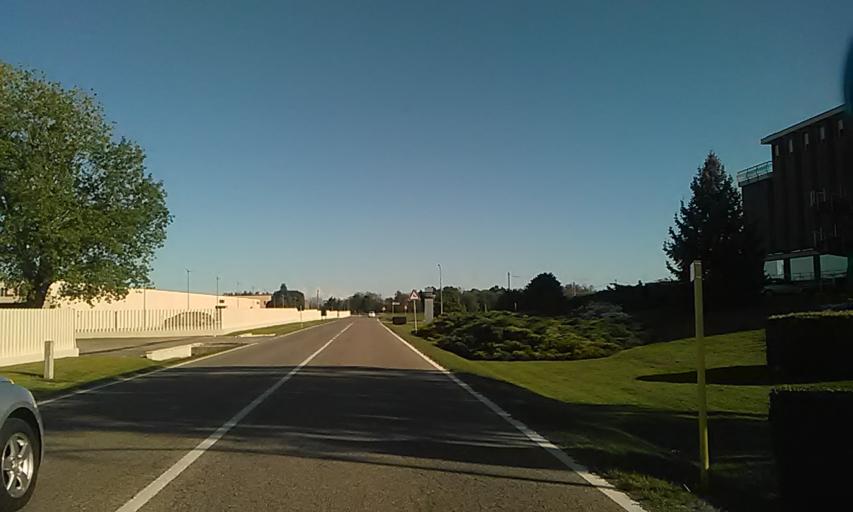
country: IT
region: Piedmont
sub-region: Provincia di Novara
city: Cavaglietto
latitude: 45.6085
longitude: 8.5230
